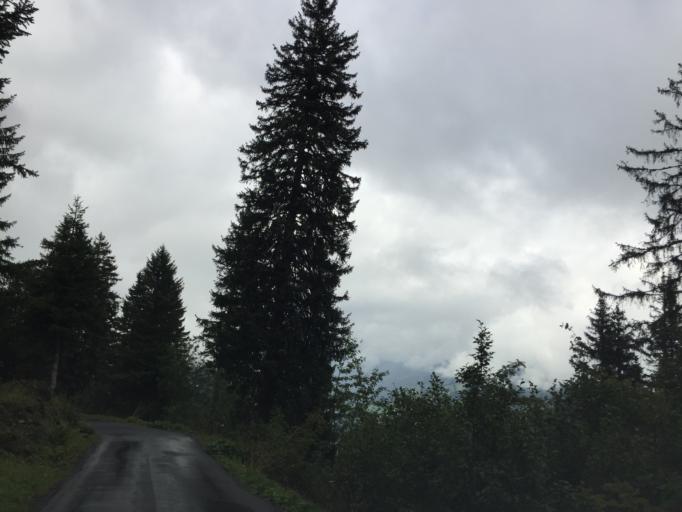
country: CH
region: Obwalden
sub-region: Obwalden
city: Sachseln
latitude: 46.7849
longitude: 8.2656
